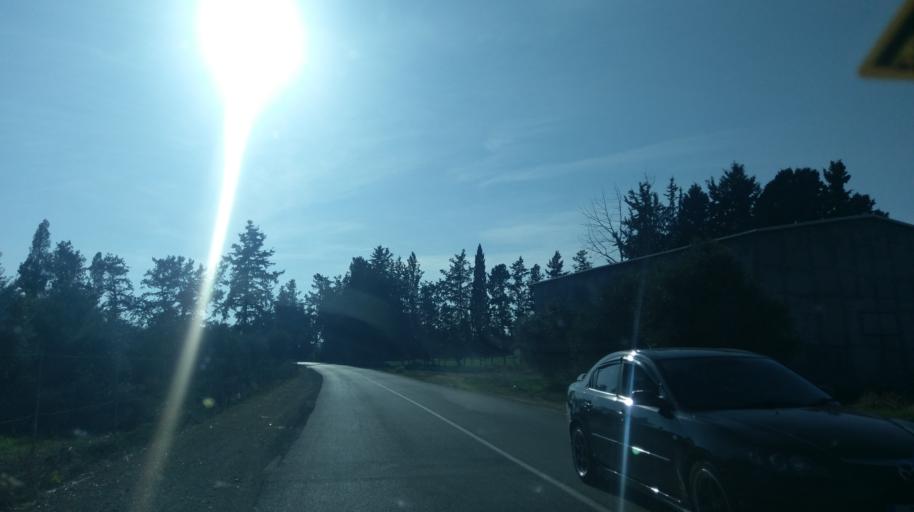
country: CY
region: Larnaka
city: Pergamos
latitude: 35.1018
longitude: 33.7267
